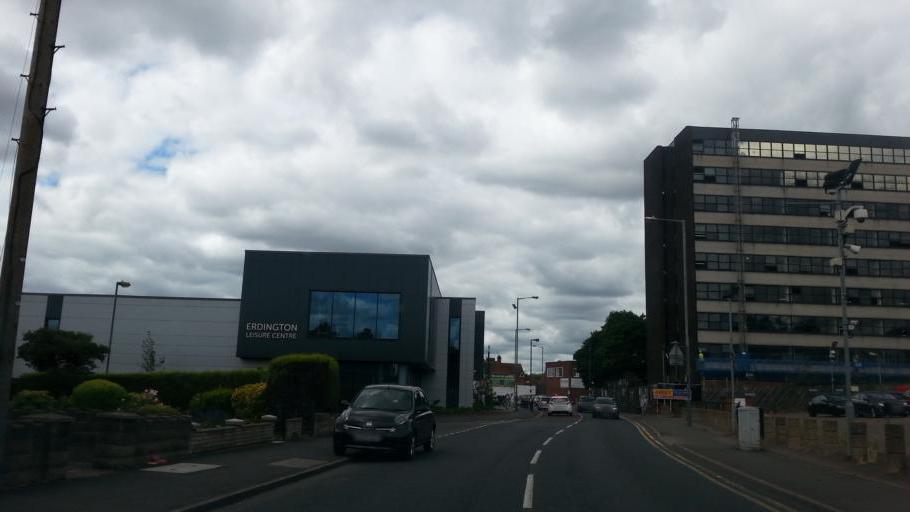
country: GB
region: England
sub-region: City and Borough of Birmingham
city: Sutton Coldfield
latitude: 52.5270
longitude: -1.8337
